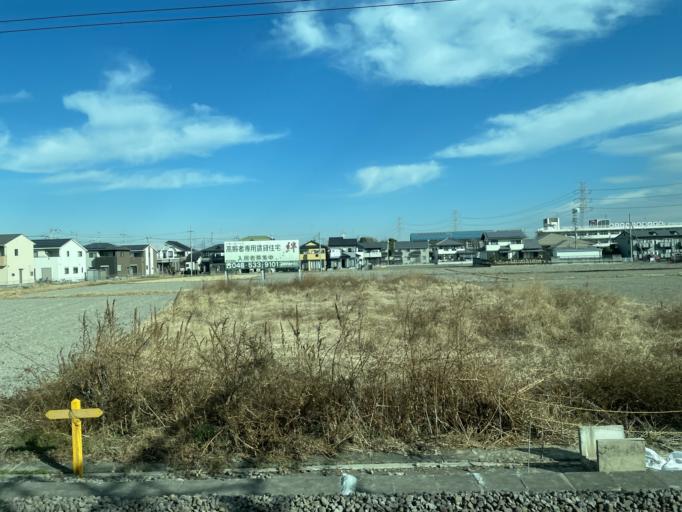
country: JP
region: Saitama
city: Fukayacho
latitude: 36.1719
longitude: 139.3357
